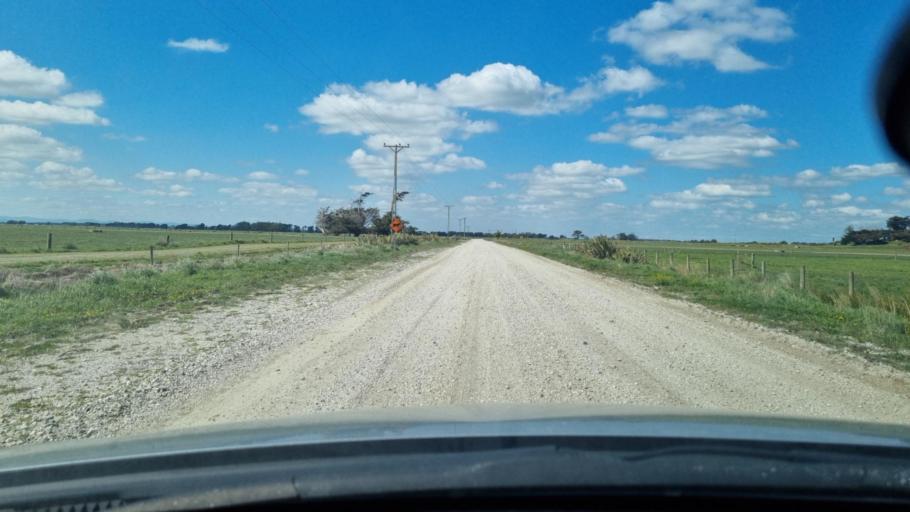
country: NZ
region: Southland
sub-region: Invercargill City
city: Invercargill
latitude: -46.3924
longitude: 168.2508
